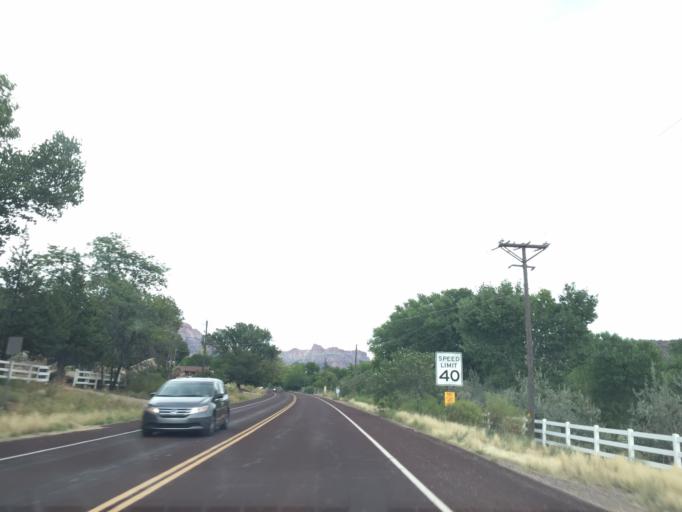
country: US
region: Utah
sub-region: Washington County
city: Hildale
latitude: 37.1610
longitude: -113.0514
